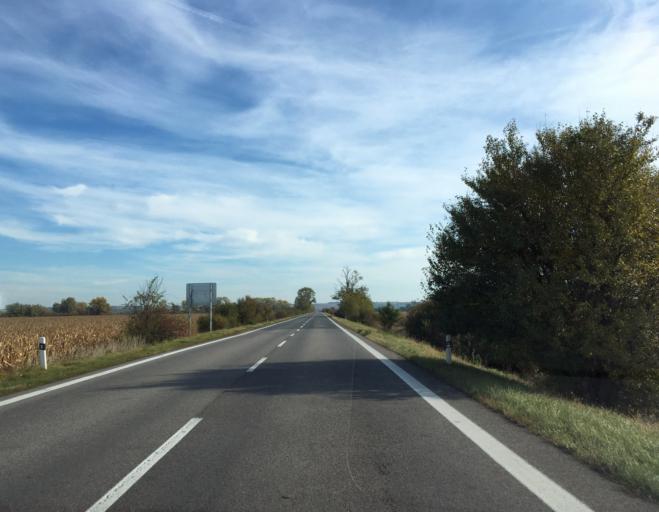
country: SK
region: Nitriansky
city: Zeliezovce
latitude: 48.1212
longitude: 18.6466
